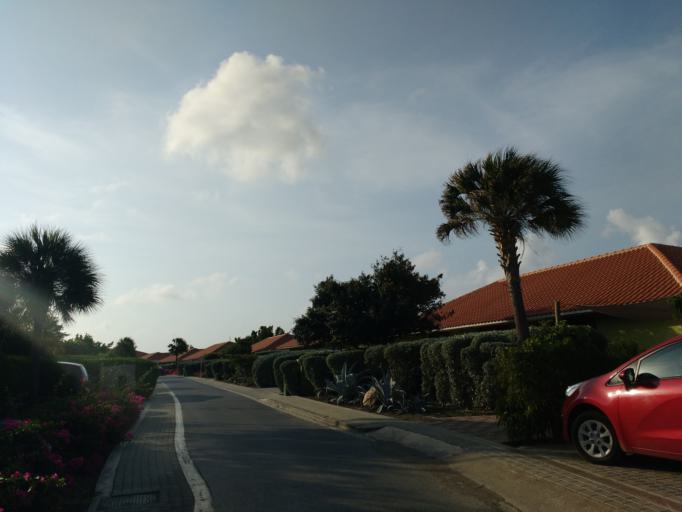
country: CW
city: Newport
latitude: 12.0736
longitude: -68.8776
